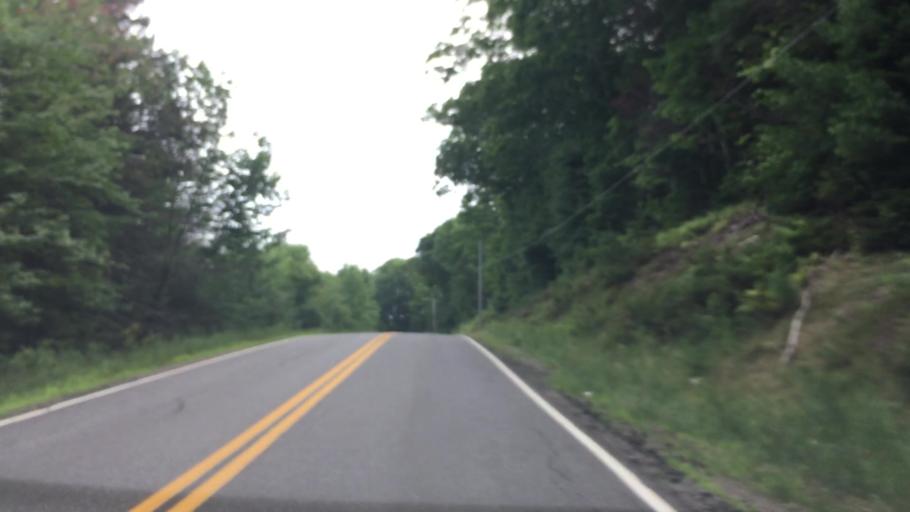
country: US
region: Maine
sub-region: Waldo County
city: Lincolnville
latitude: 44.3498
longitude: -69.0556
